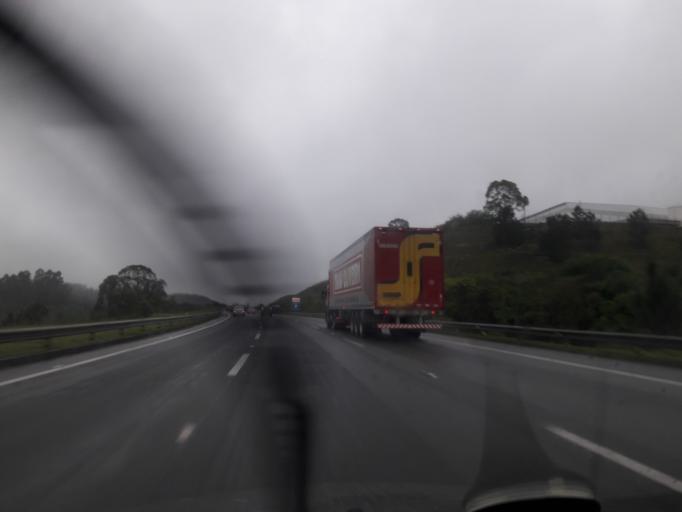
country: BR
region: Sao Paulo
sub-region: Embu
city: Embu
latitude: -23.6559
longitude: -46.8305
